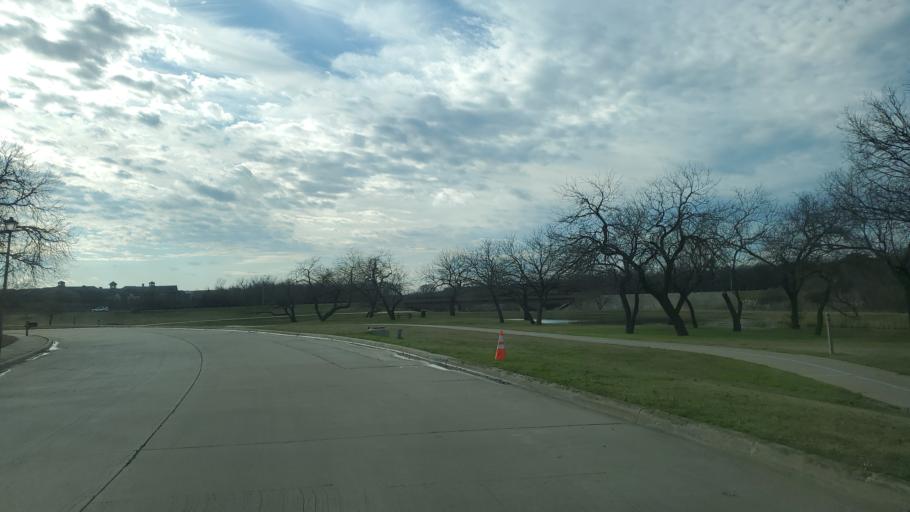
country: US
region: Texas
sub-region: Dallas County
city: Carrollton
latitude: 32.9902
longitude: -96.8997
